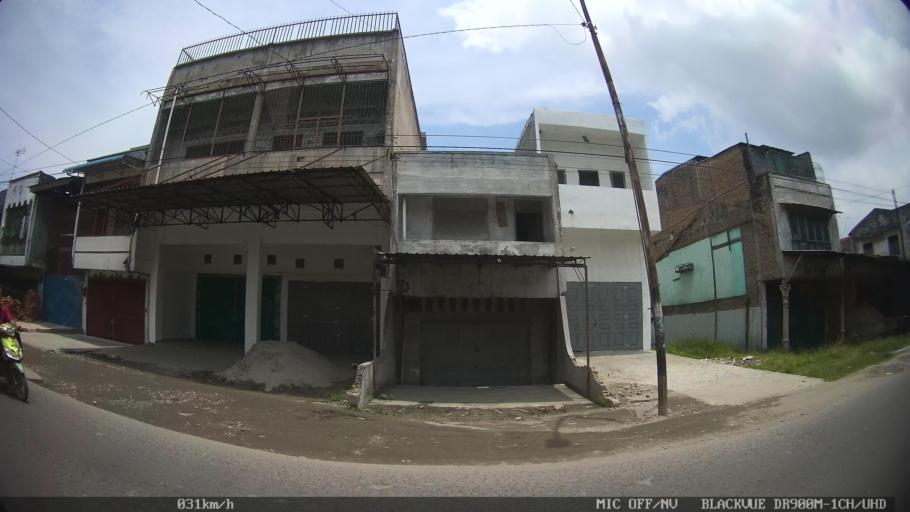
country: ID
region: North Sumatra
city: Labuhan Deli
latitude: 3.6858
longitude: 98.6675
